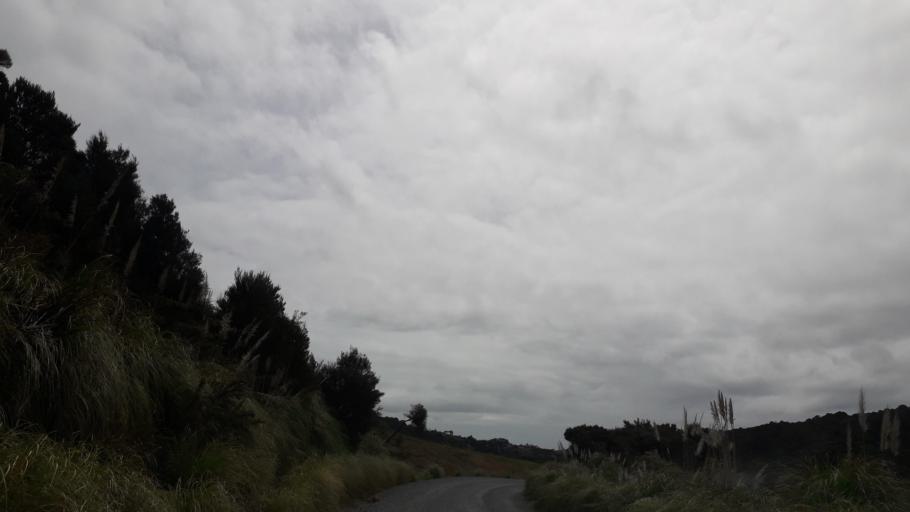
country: NZ
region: Northland
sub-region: Far North District
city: Taipa
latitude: -35.0165
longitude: 173.5507
